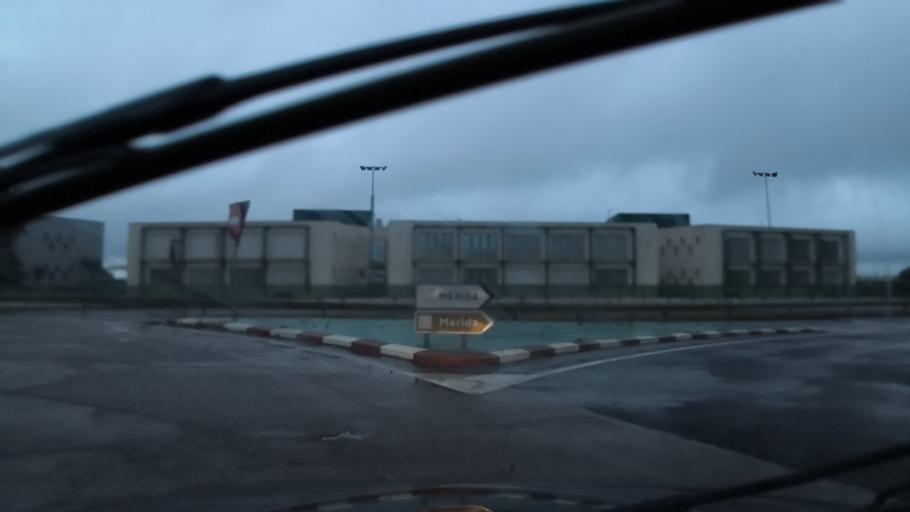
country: ES
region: Extremadura
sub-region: Provincia de Badajoz
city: Merida
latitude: 38.9050
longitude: -6.3669
